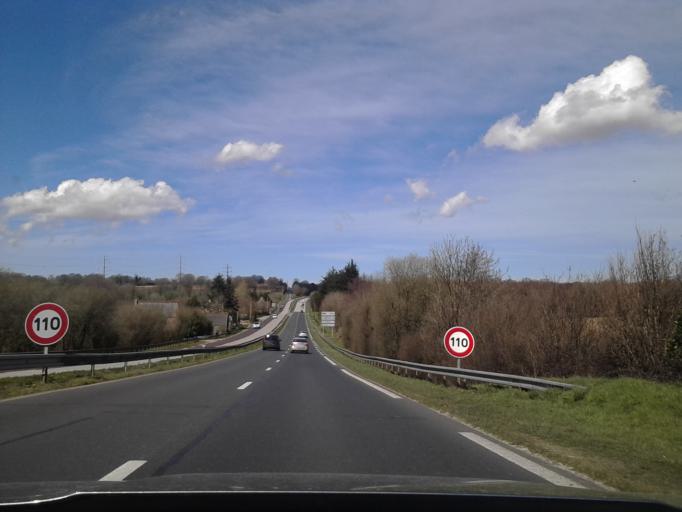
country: FR
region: Lower Normandy
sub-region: Departement de la Manche
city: Brix
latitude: 49.5543
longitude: -1.5623
